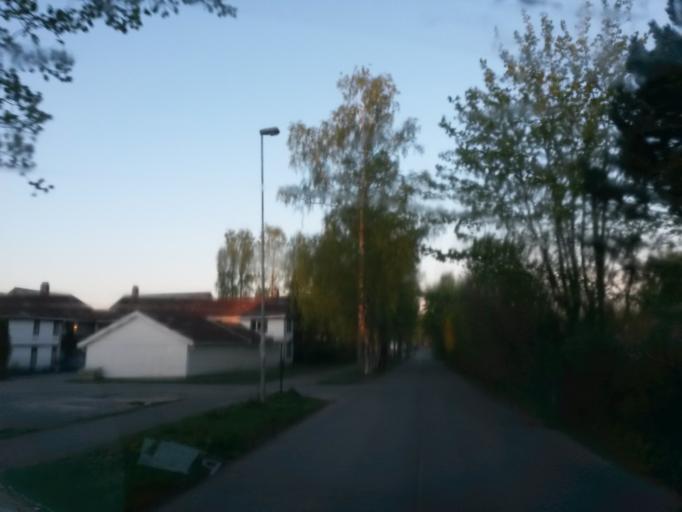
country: NO
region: Akershus
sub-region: Asker
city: Asker
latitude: 59.8324
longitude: 10.4091
